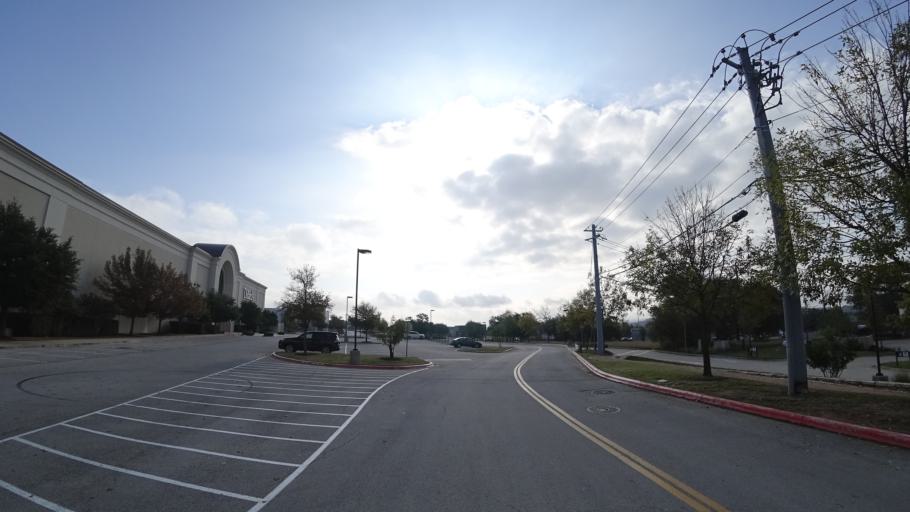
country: US
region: Texas
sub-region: Travis County
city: Bee Cave
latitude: 30.3101
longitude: -97.9447
